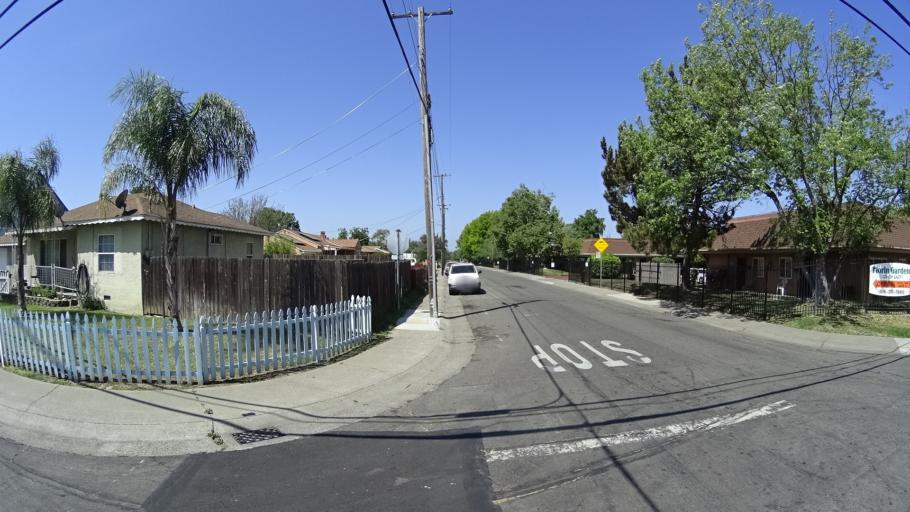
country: US
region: California
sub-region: Sacramento County
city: Parkway
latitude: 38.4995
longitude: -121.4791
